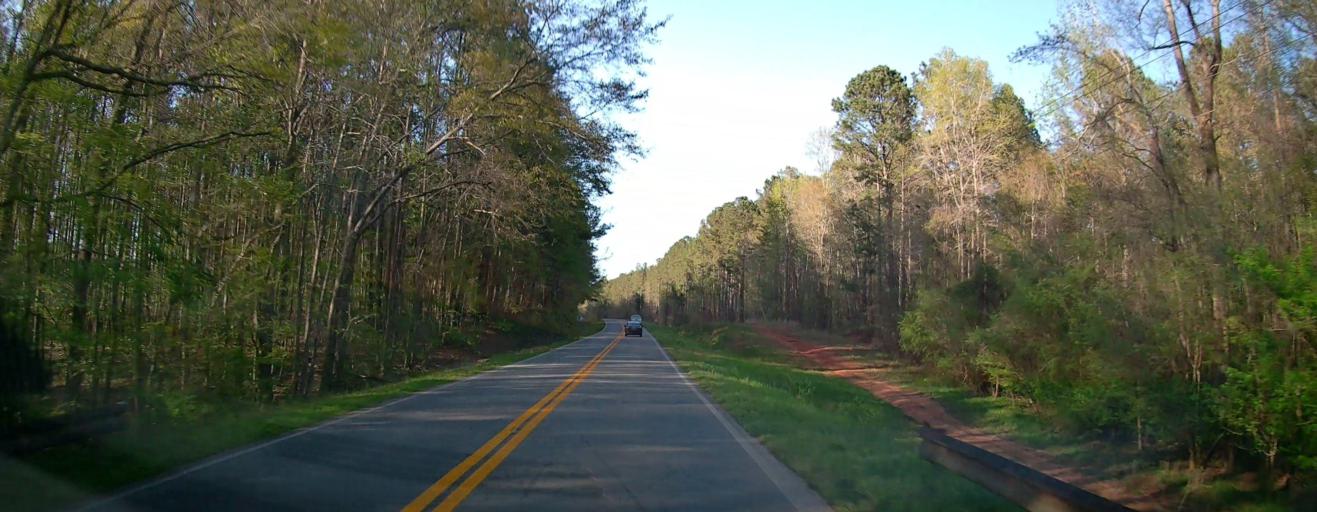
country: US
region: Georgia
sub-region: Butts County
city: Jackson
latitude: 33.3113
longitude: -83.9034
